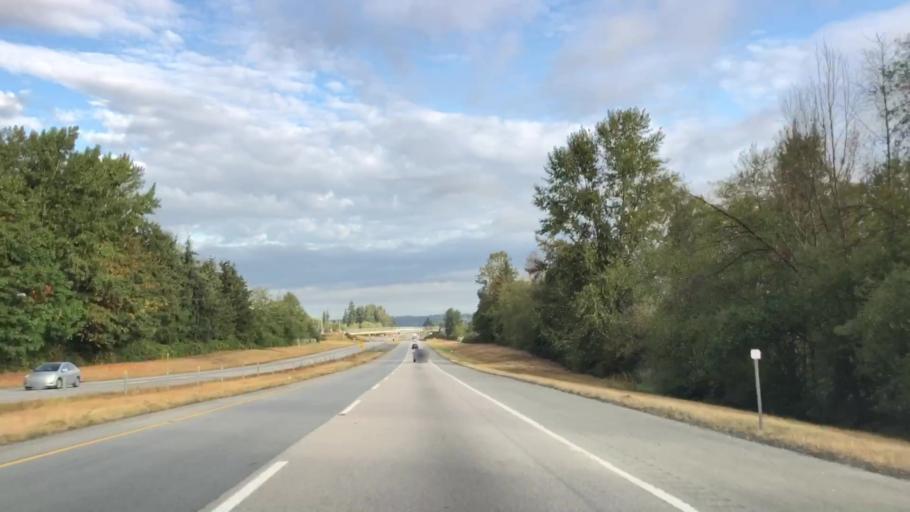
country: CA
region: British Columbia
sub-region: Greater Vancouver Regional District
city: White Rock
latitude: 49.0554
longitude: -122.7968
